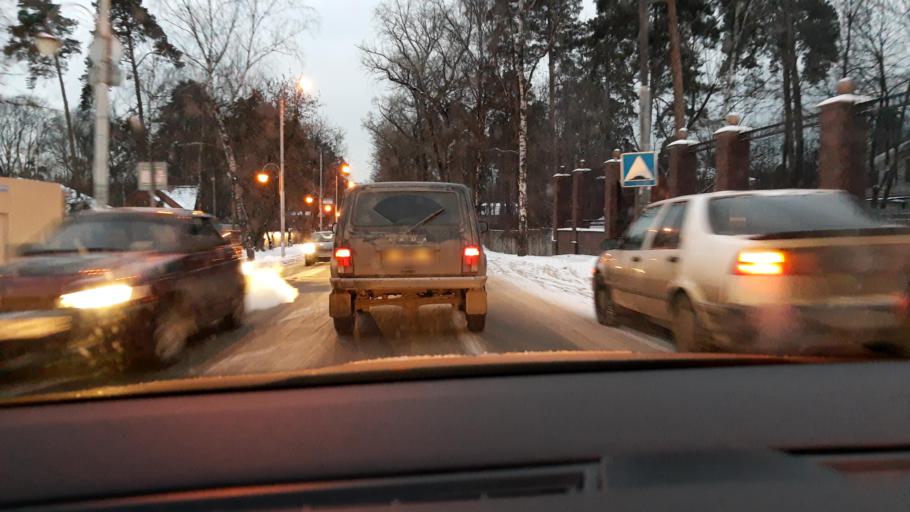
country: RU
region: Moskovskaya
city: Tomilino
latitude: 55.6549
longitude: 37.9520
